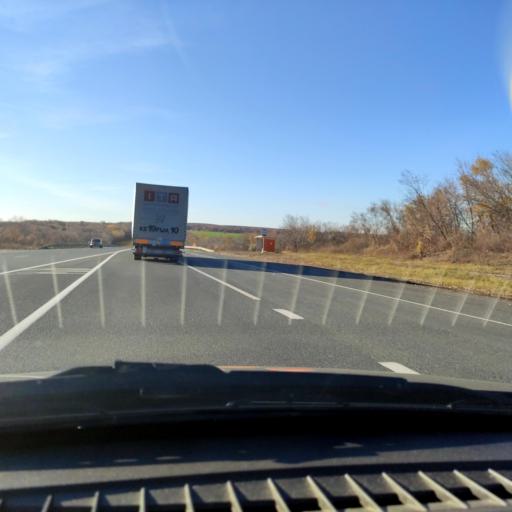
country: RU
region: Samara
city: Mezhdurechensk
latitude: 53.2564
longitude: 49.1261
